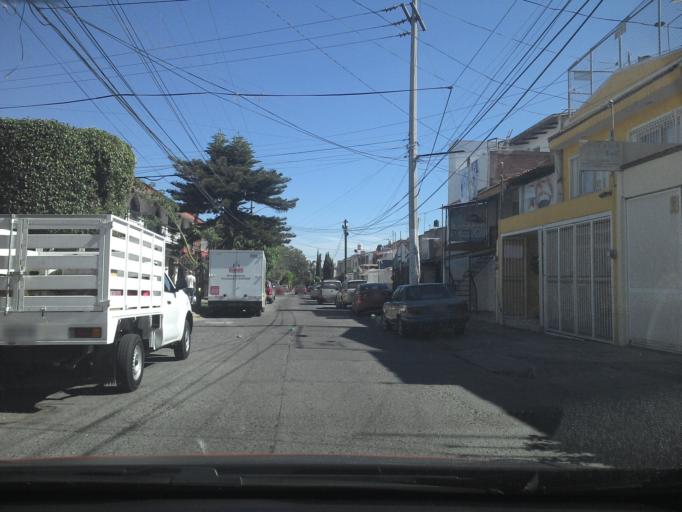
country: MX
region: Jalisco
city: Zapopan2
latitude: 20.7447
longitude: -103.4040
